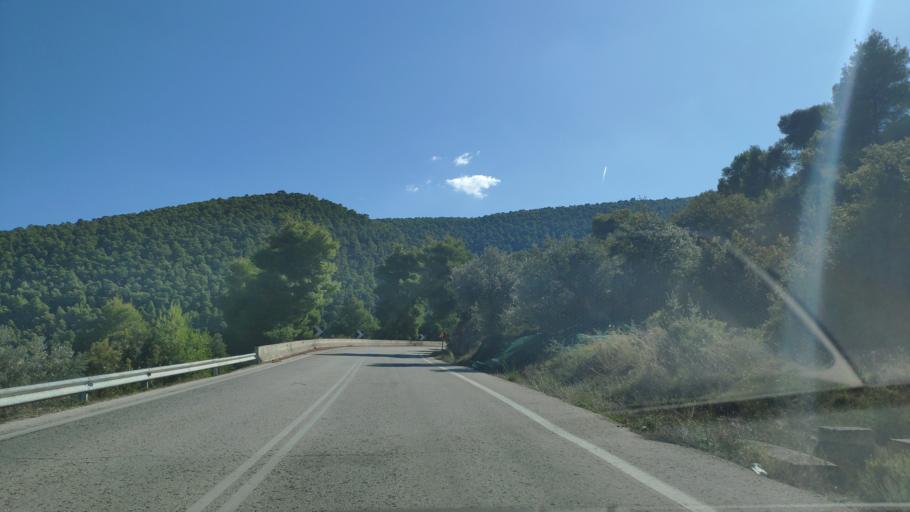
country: GR
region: Peloponnese
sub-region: Nomos Korinthias
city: Sofikon
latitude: 37.8277
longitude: 23.0806
